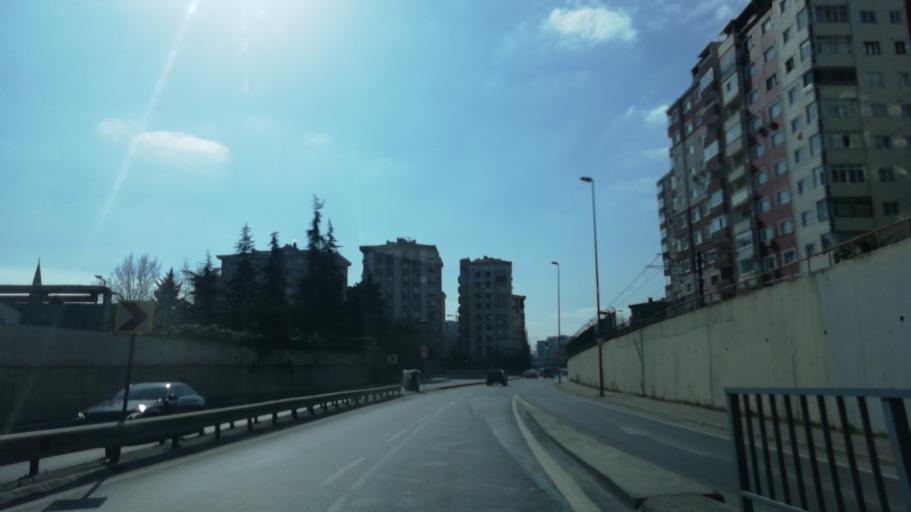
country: TR
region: Istanbul
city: merter keresteciler
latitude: 41.0185
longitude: 28.9009
